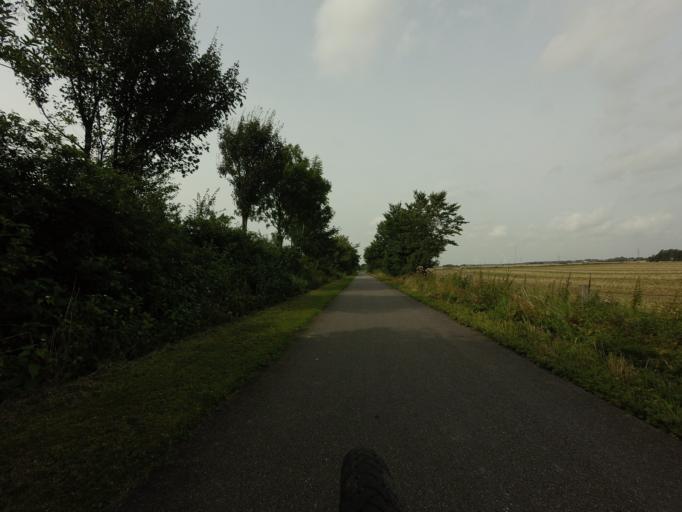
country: DK
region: Zealand
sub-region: Naestved Kommune
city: Naestved
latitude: 55.2563
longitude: 11.6572
